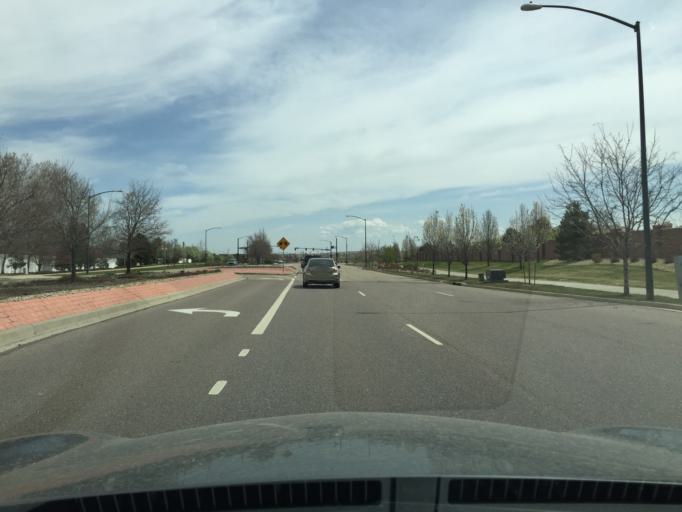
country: US
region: Colorado
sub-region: Adams County
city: Northglenn
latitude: 39.9575
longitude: -104.9999
